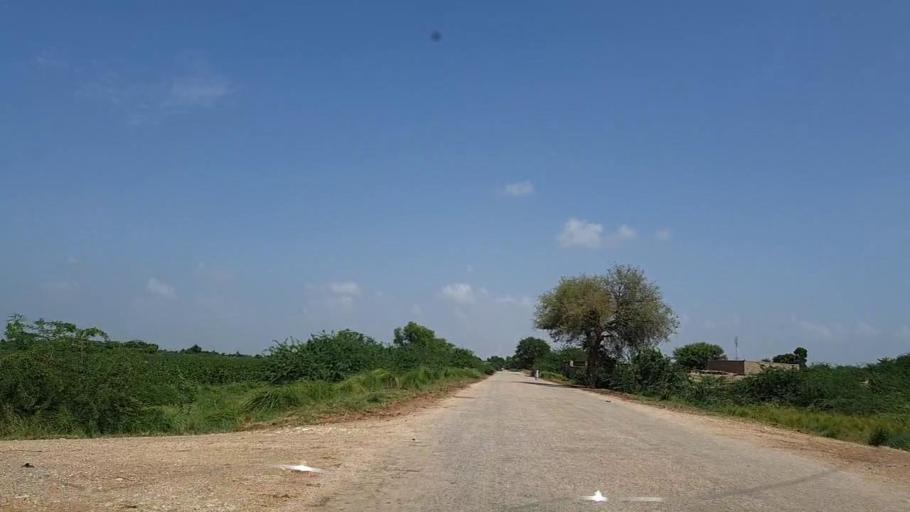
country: PK
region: Sindh
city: Pad Idan
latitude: 26.7950
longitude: 68.2420
